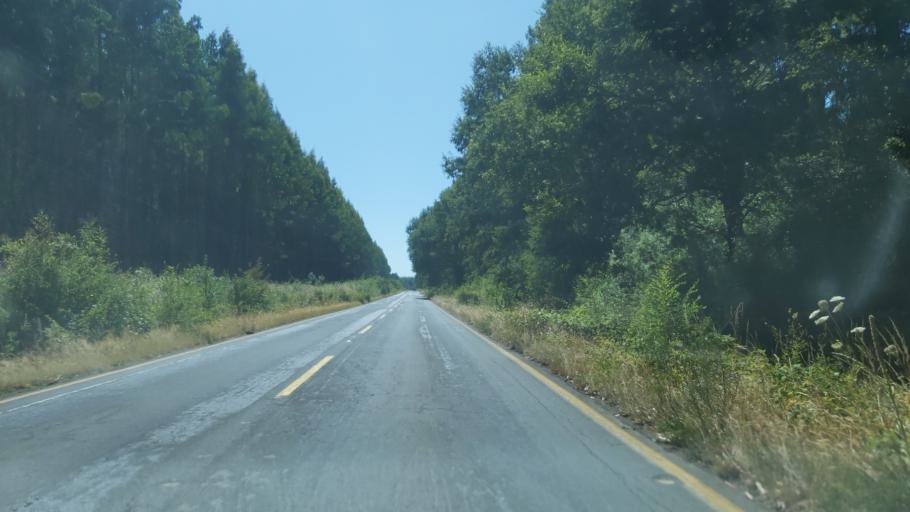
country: CL
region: Araucania
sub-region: Provincia de Malleco
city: Victoria
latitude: -38.2969
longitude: -72.1344
